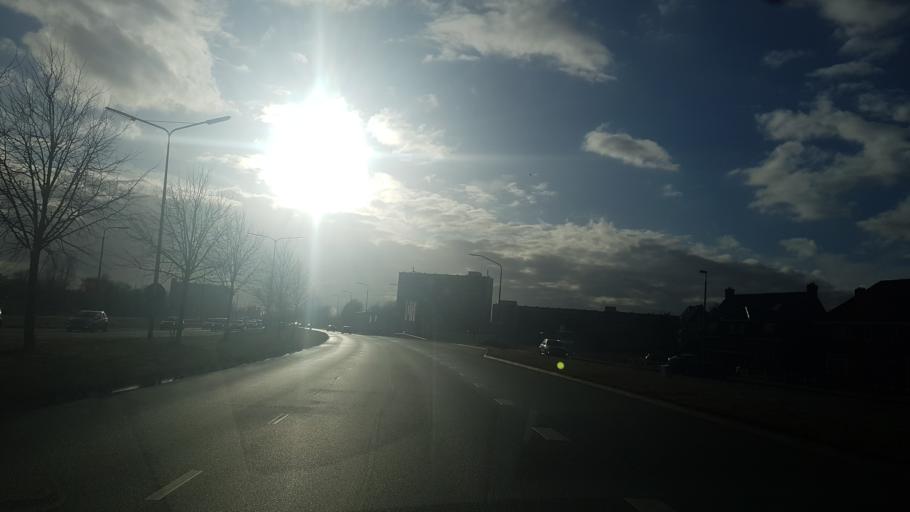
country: NL
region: Friesland
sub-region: Gemeente Leeuwarden
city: Camminghaburen
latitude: 53.2170
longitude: 5.8273
